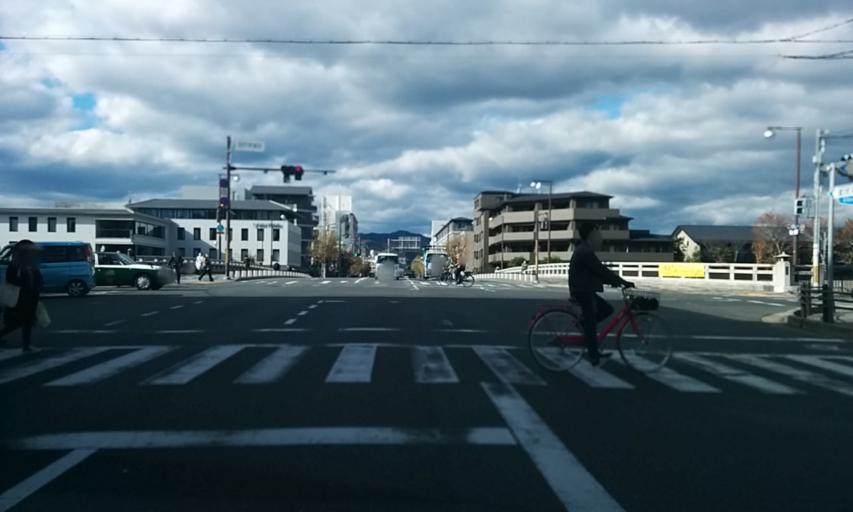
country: JP
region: Kyoto
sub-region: Kyoto-shi
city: Kamigyo-ku
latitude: 35.0424
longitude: 135.7798
